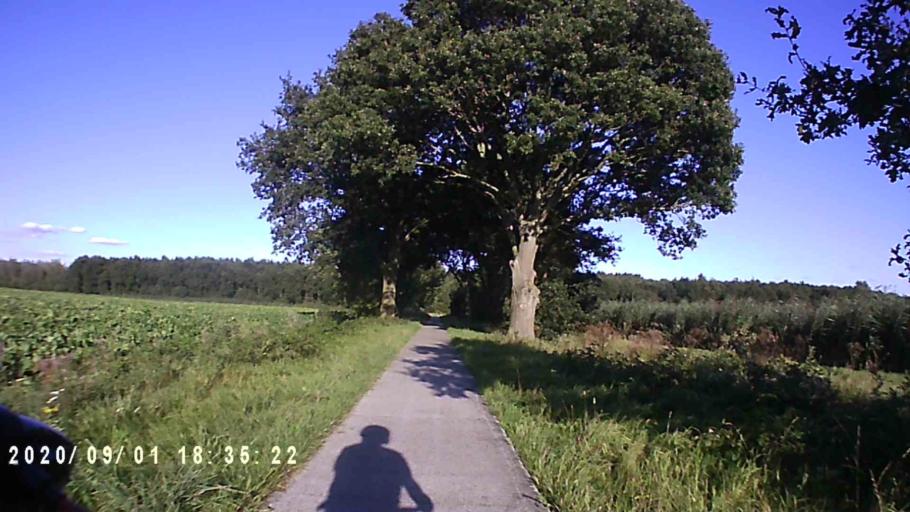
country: NL
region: Groningen
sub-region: Gemeente Hoogezand-Sappemeer
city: Sappemeer
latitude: 53.1495
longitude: 6.8049
